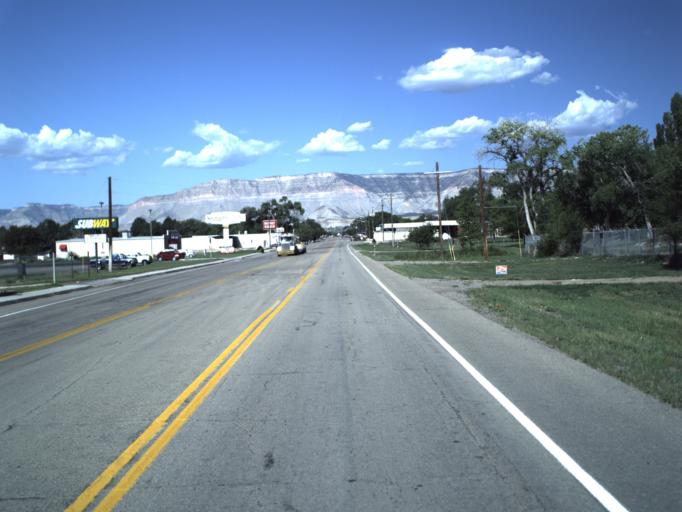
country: US
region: Utah
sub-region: Emery County
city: Castle Dale
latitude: 39.2119
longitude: -111.0061
